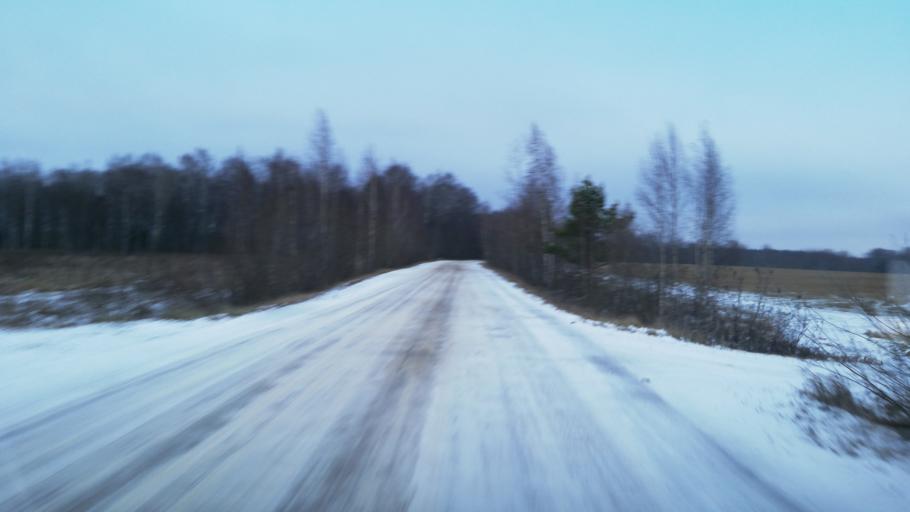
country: RU
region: Kostroma
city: Krasnoye-na-Volge
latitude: 57.6886
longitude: 41.1808
